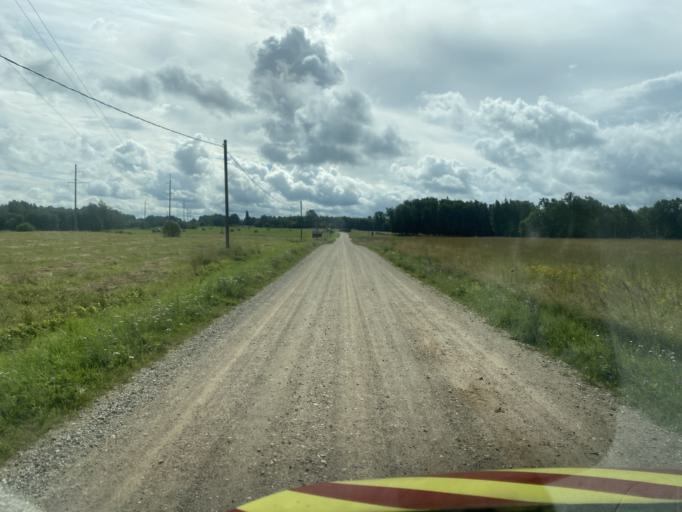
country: EE
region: Viljandimaa
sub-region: Karksi vald
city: Karksi-Nuia
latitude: 58.0897
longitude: 25.4856
